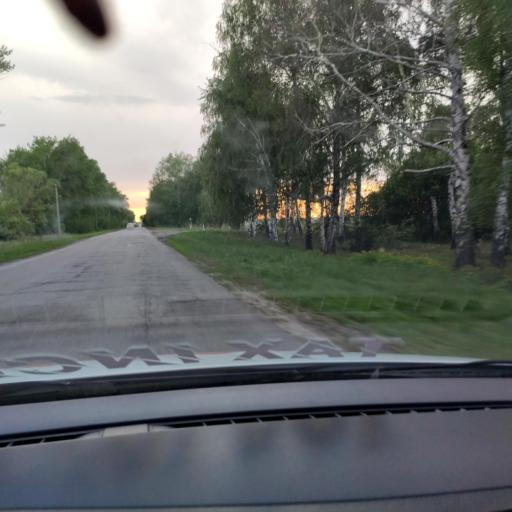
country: RU
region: Voronezj
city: Maslovka
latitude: 51.4405
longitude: 39.2809
